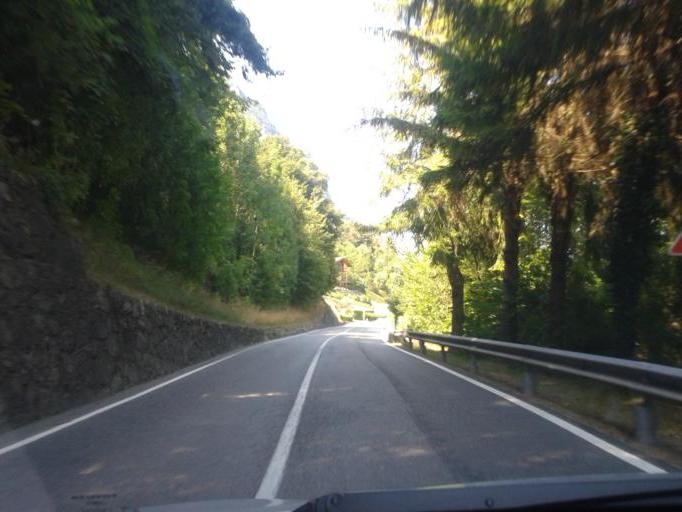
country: IT
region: Lombardy
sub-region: Provincia di Brescia
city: Crone
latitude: 45.7443
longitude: 10.4725
